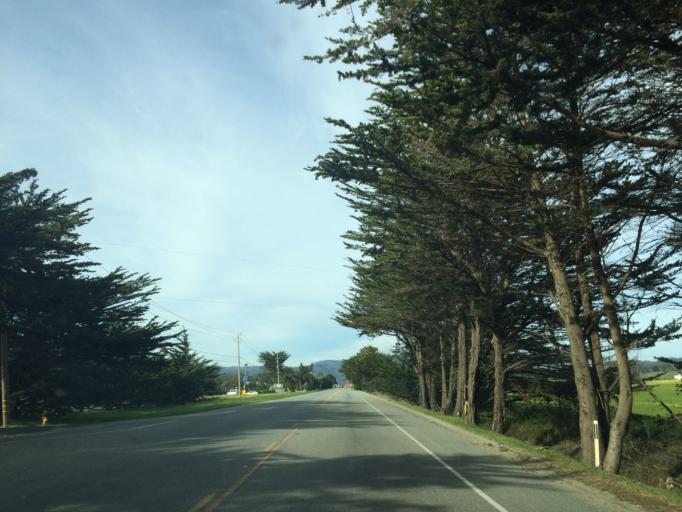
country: US
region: California
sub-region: San Mateo County
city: Half Moon Bay
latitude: 37.4410
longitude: -122.4278
